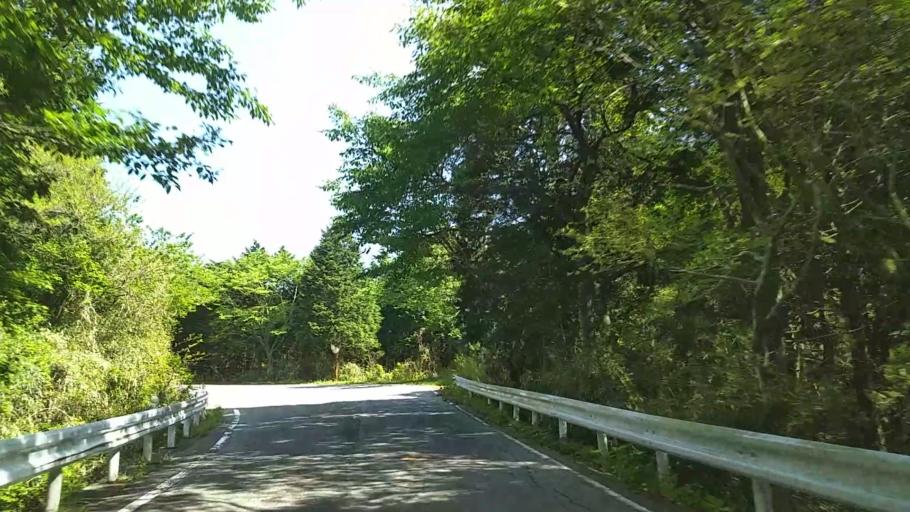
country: JP
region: Shizuoka
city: Gotemba
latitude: 35.2722
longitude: 138.9594
